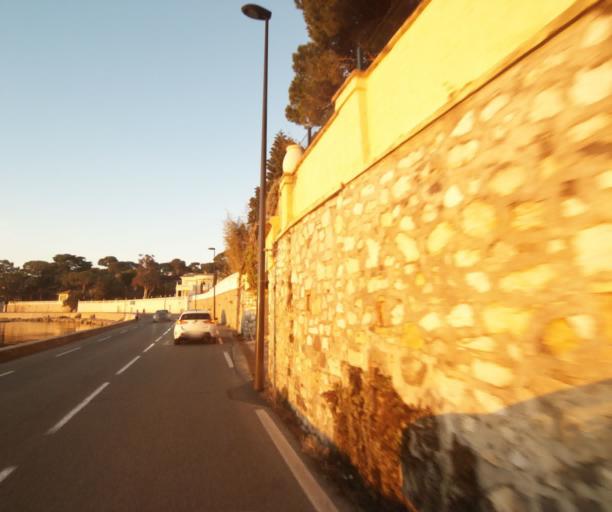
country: FR
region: Provence-Alpes-Cote d'Azur
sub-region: Departement des Alpes-Maritimes
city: Antibes
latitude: 43.5587
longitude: 7.1219
